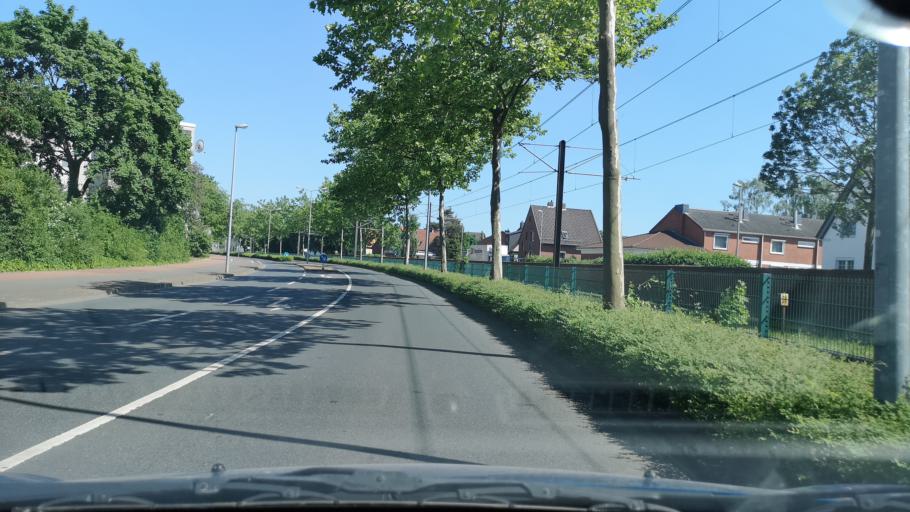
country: DE
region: Lower Saxony
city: Auf der Horst
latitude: 52.4173
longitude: 9.5982
